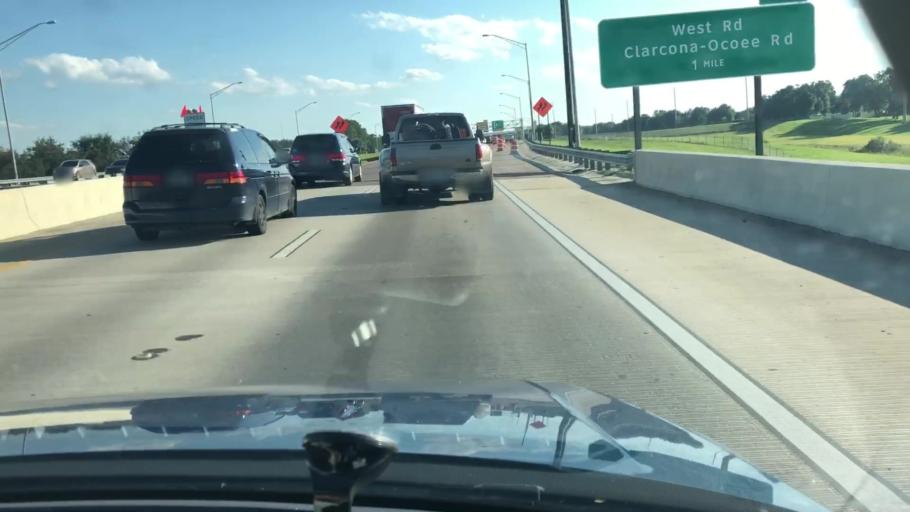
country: US
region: Florida
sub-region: Orange County
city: Paradise Heights
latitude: 28.6217
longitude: -81.5364
